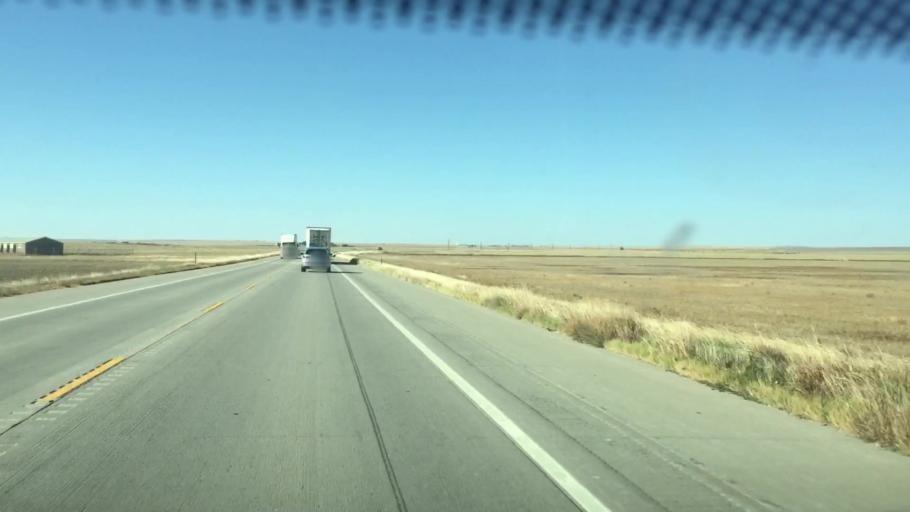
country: US
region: Colorado
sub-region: Kiowa County
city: Eads
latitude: 38.3708
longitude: -102.7273
